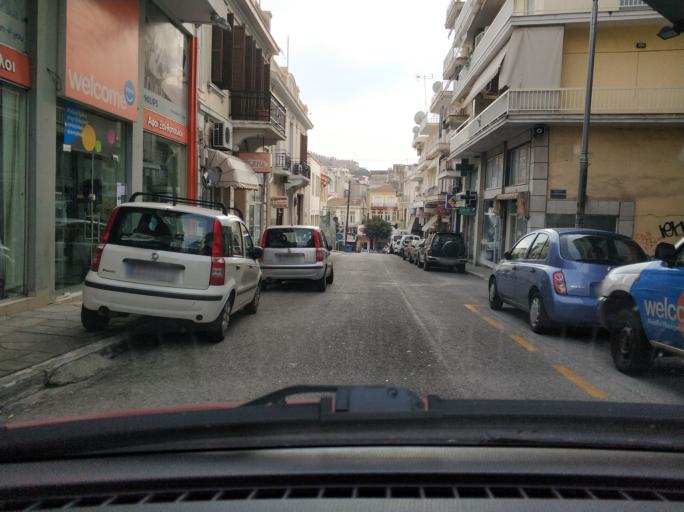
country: GR
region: East Macedonia and Thrace
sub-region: Nomos Kavalas
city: Kavala
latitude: 40.9376
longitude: 24.4146
